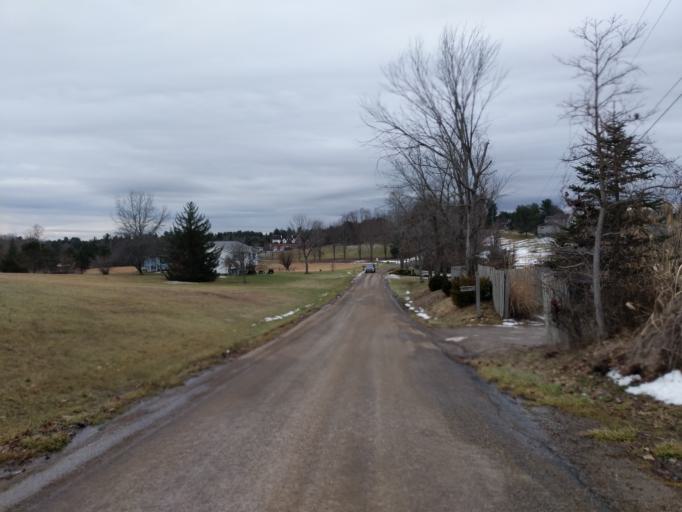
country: US
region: Ohio
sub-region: Athens County
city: The Plains
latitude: 39.3207
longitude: -82.1577
